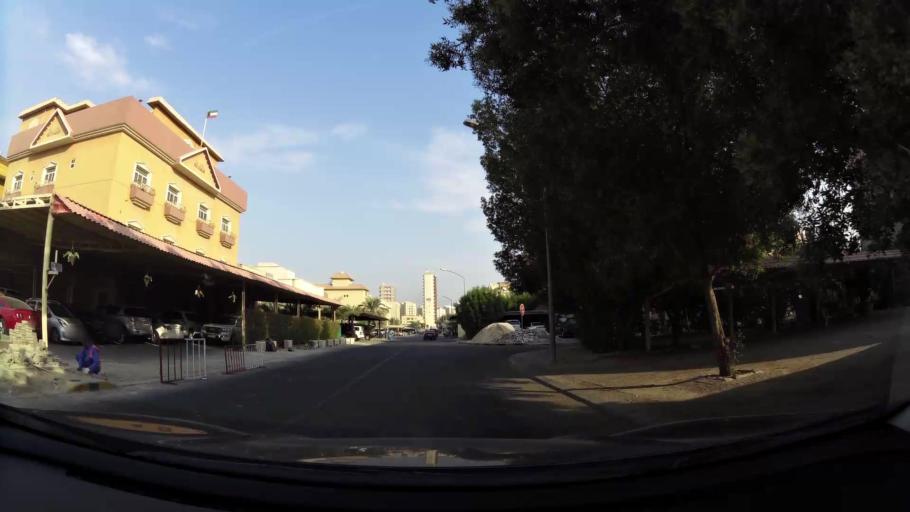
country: KW
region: Muhafazat Hawalli
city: Ar Rumaythiyah
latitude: 29.3215
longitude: 48.0725
